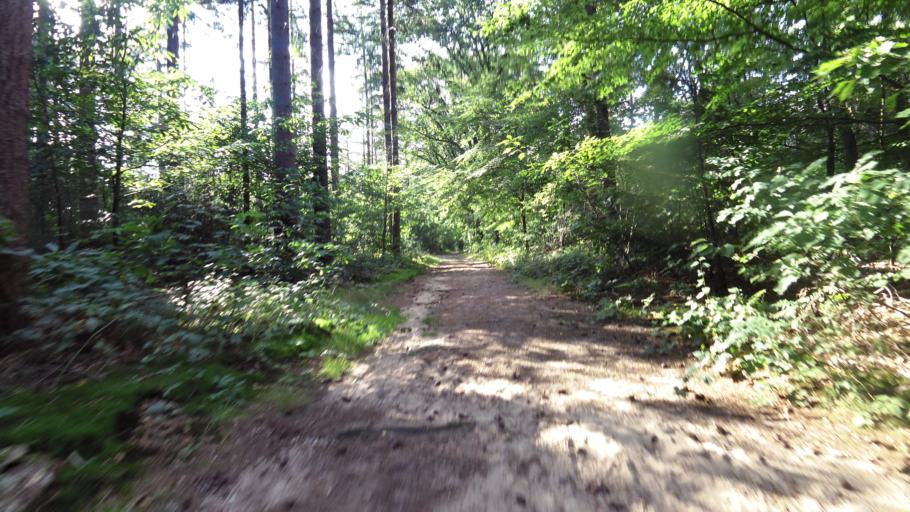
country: NL
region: Gelderland
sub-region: Gemeente Renkum
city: Renkum
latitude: 51.9978
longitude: 5.7179
